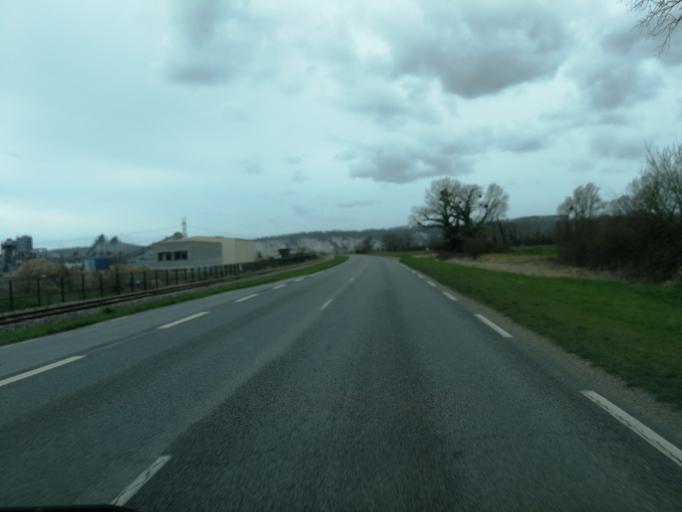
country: FR
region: Haute-Normandie
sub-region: Departement de l'Eure
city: Quillebeuf-sur-Seine
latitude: 49.4891
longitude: 0.5071
